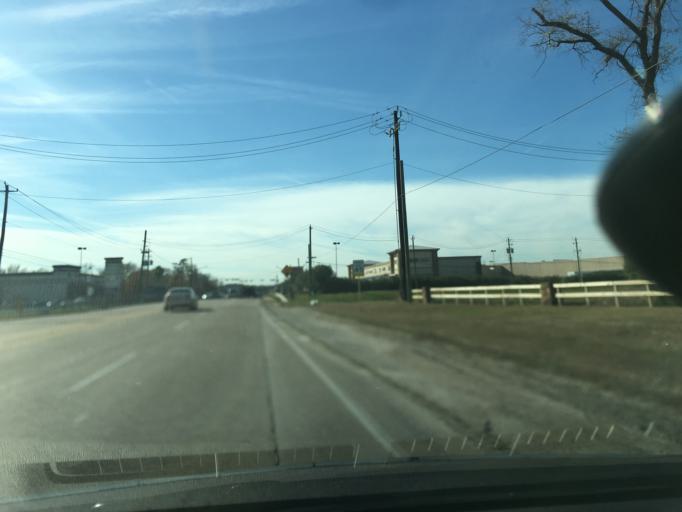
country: US
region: Texas
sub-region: Harris County
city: Cloverleaf
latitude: 29.8102
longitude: -95.1579
